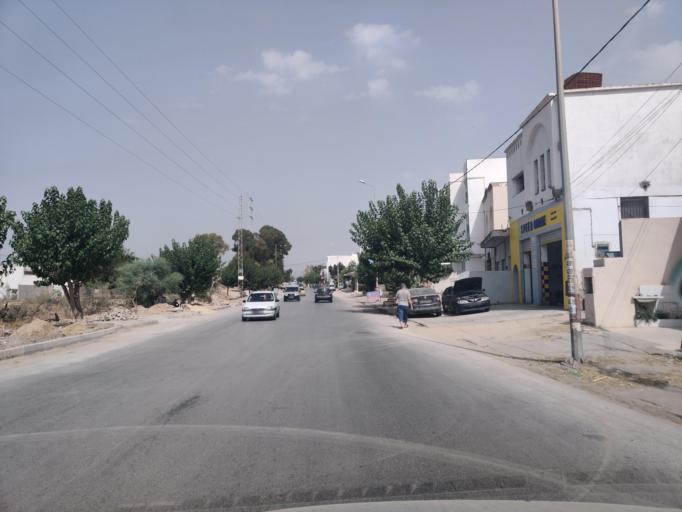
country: TN
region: Nabul
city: Al Hammamat
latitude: 36.4154
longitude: 10.5954
